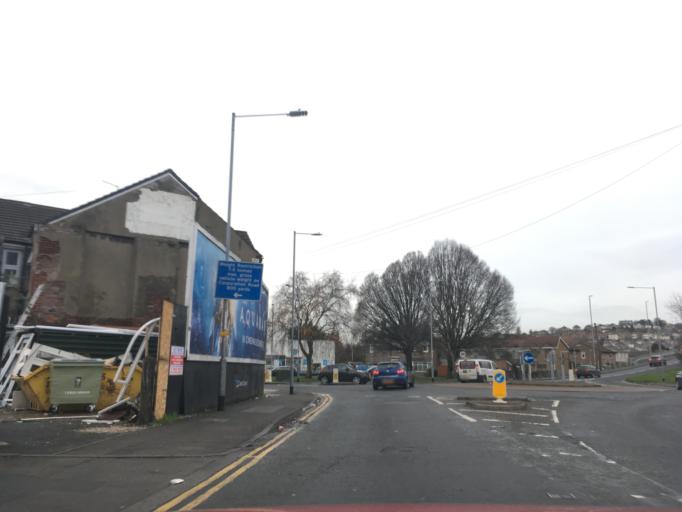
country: GB
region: Wales
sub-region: Newport
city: Caerleon
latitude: 51.5825
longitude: -2.9626
